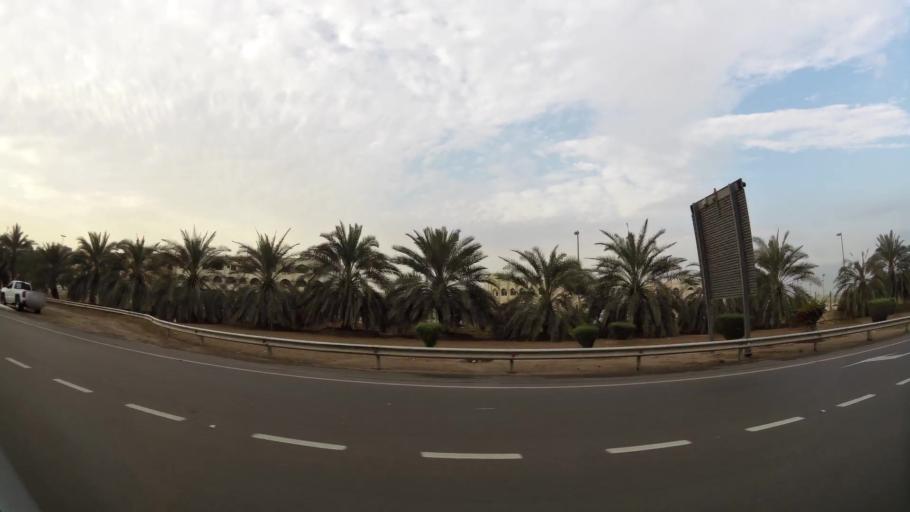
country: AE
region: Abu Dhabi
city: Abu Dhabi
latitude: 24.2835
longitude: 54.6444
